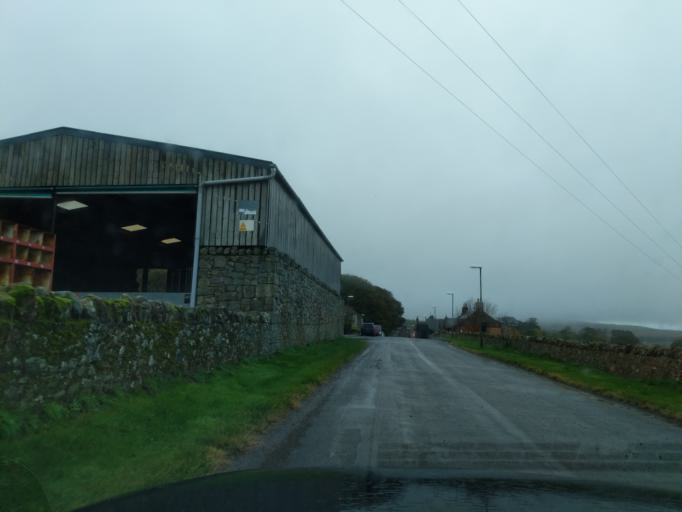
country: GB
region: Scotland
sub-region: East Lothian
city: Dunbar
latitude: 55.9570
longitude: -2.4425
